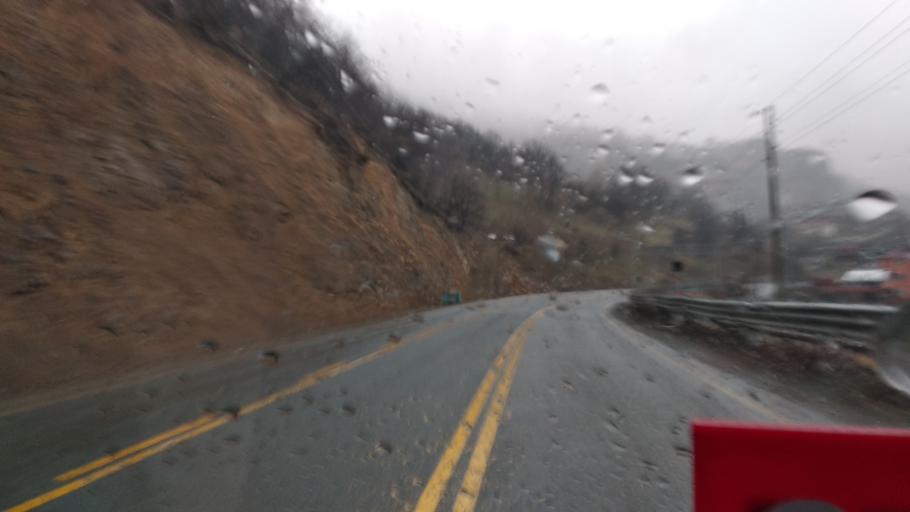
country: TR
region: Trabzon
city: Macka
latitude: 40.7077
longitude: 39.4939
